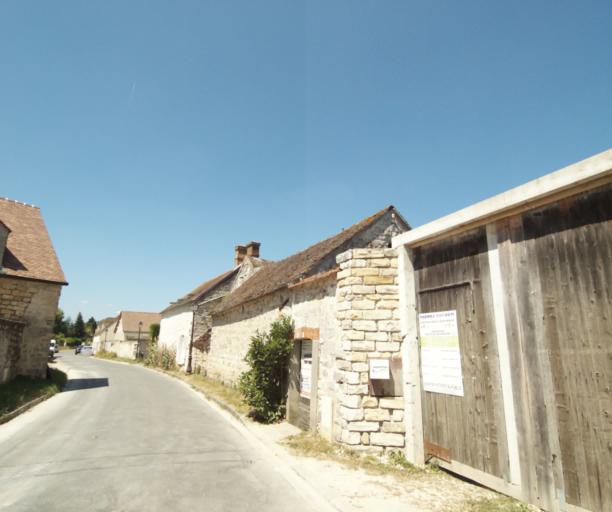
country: FR
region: Ile-de-France
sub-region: Departement de Seine-et-Marne
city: Noisy-sur-Ecole
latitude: 48.3714
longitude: 2.4987
